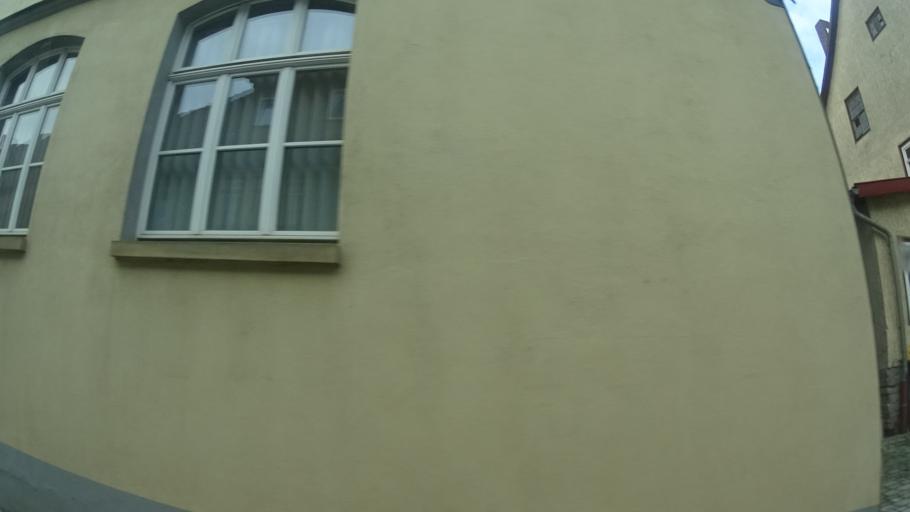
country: DE
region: Thuringia
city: Romhild
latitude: 50.3970
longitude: 10.5387
